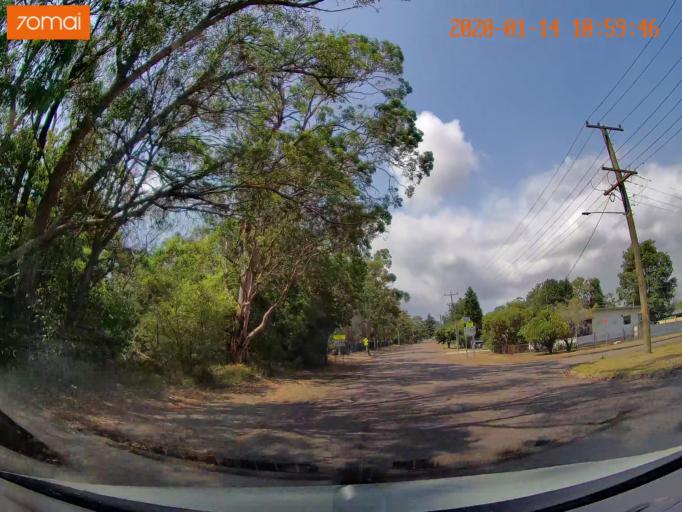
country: AU
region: New South Wales
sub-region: Lake Macquarie Shire
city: Dora Creek
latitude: -33.1022
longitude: 151.4884
